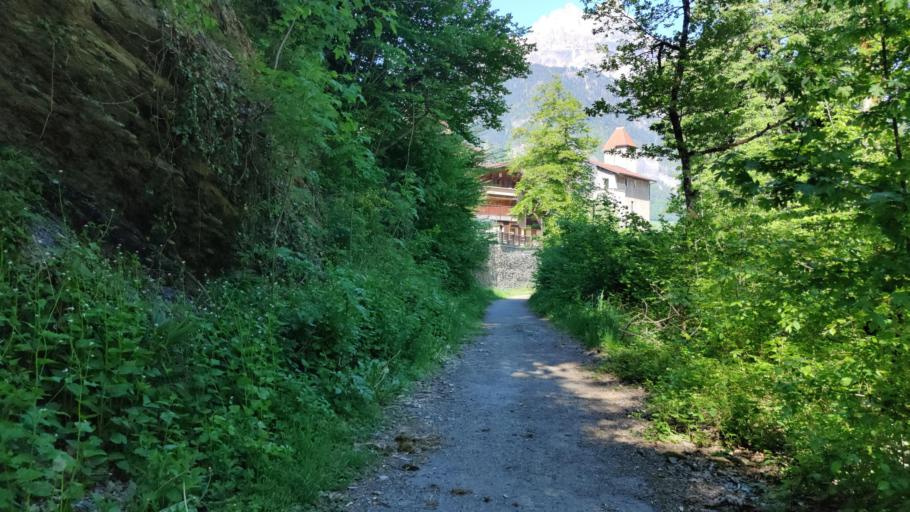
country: FR
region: Rhone-Alpes
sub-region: Departement de la Haute-Savoie
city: Sallanches
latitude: 45.9350
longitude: 6.6232
